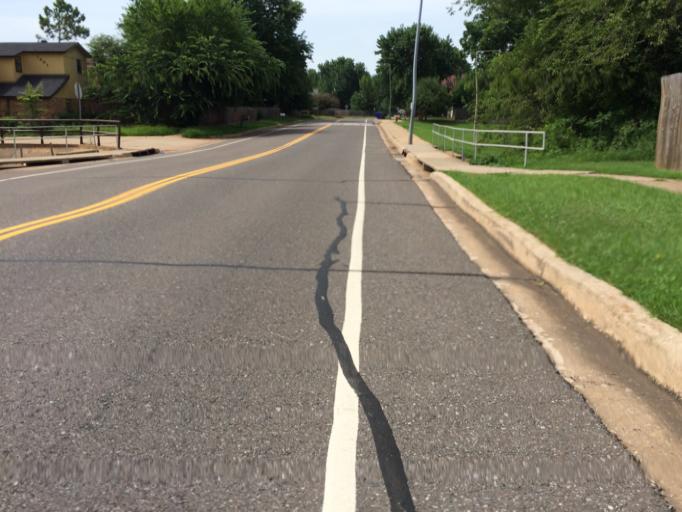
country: US
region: Oklahoma
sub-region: Cleveland County
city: Norman
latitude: 35.1958
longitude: -97.4109
